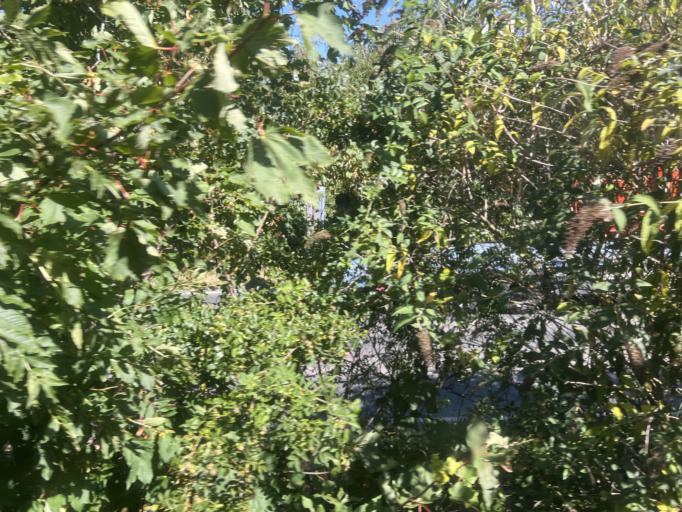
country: GB
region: England
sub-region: Lincolnshire
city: Kirton
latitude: 52.9761
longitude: -0.1218
